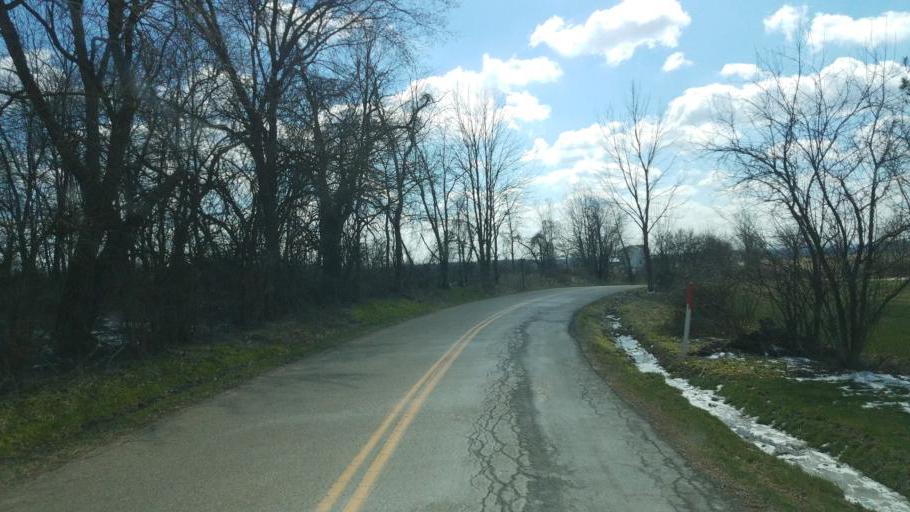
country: US
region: Ohio
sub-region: Knox County
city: Mount Vernon
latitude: 40.3364
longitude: -82.5434
